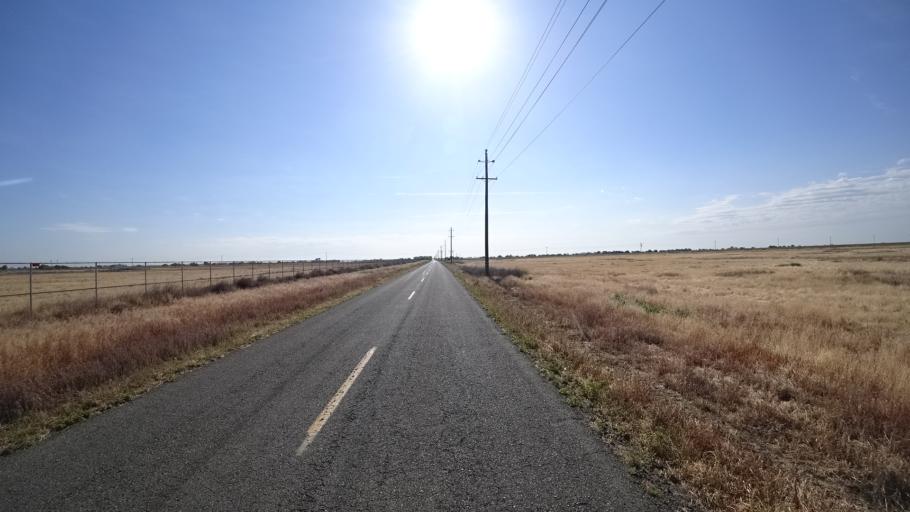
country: US
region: California
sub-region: Kings County
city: Lemoore
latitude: 36.2256
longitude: -119.7485
